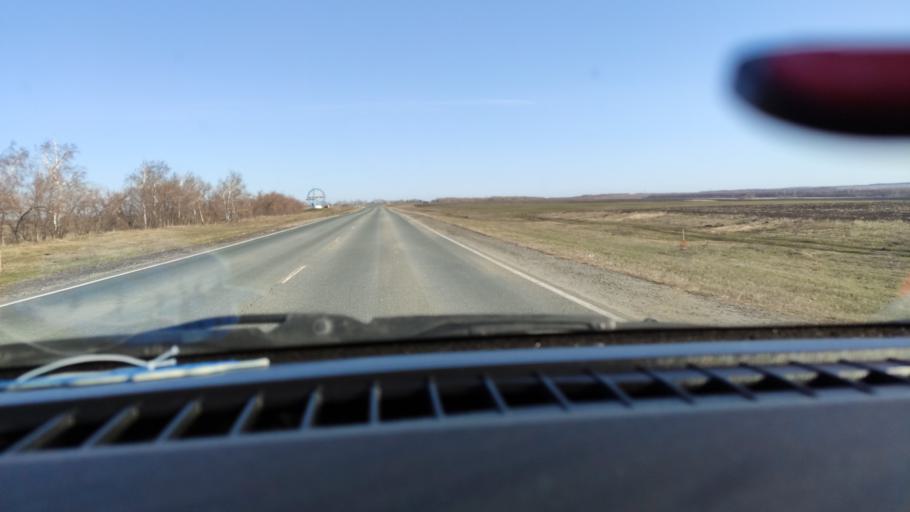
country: RU
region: Saratov
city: Dukhovnitskoye
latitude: 52.8007
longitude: 48.2297
